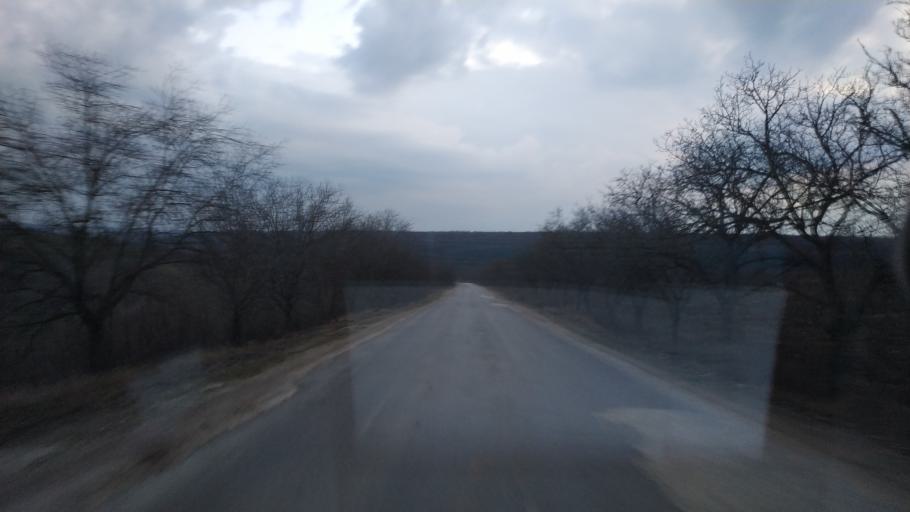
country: MD
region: Anenii Noi
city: Anenii Noi
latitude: 46.9552
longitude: 29.2830
